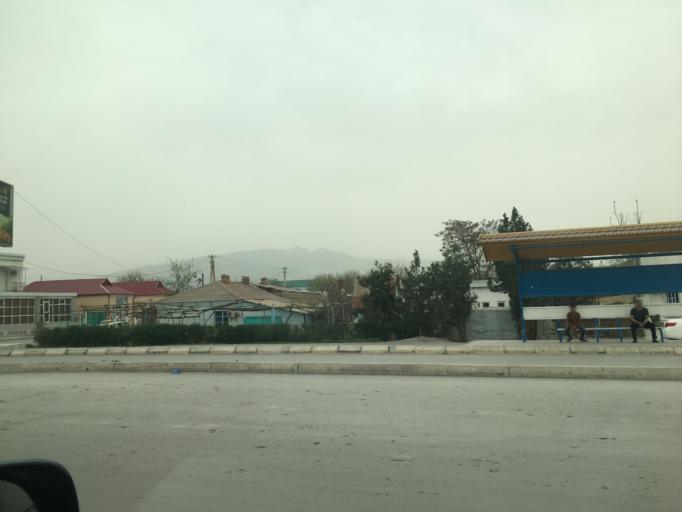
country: TM
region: Ahal
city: Abadan
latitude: 38.1608
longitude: 57.9614
